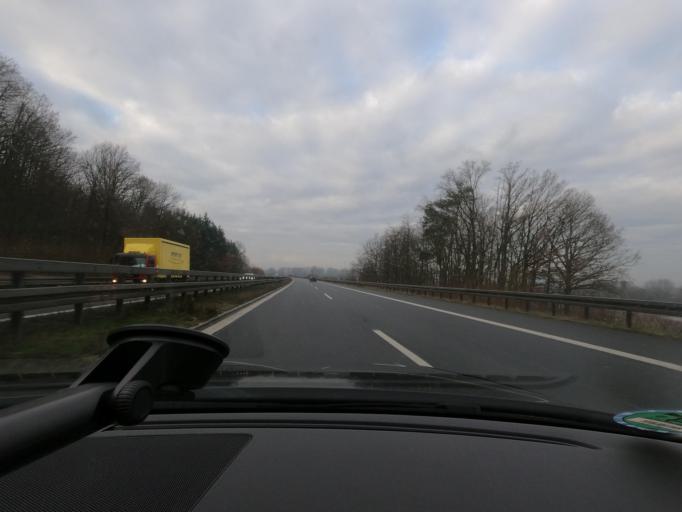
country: DE
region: Bavaria
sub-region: Upper Franconia
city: Zapfendorf
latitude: 50.0053
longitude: 10.9238
